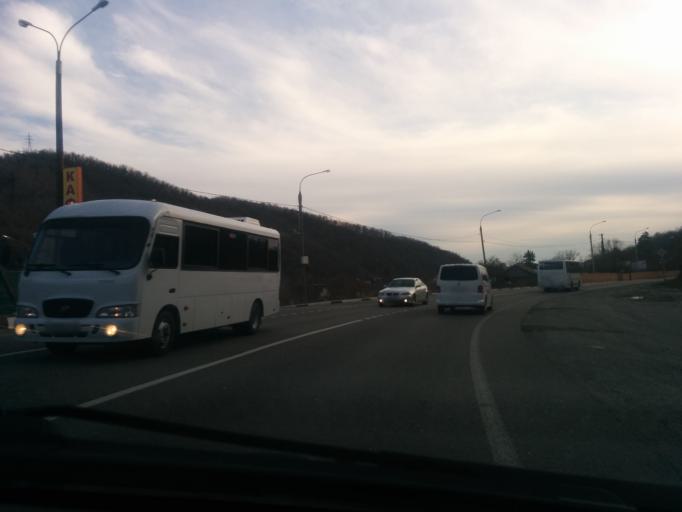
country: RU
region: Krasnodarskiy
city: Ol'ginka
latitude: 44.2138
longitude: 38.8948
